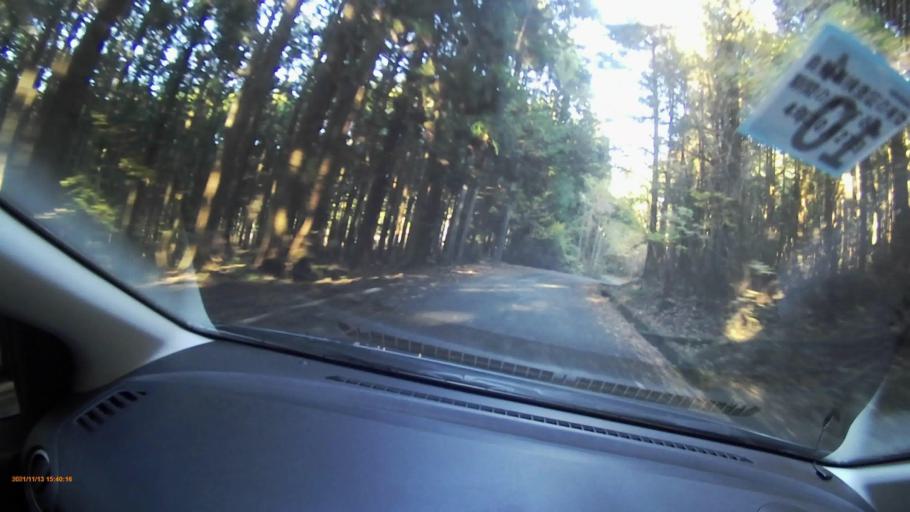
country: JP
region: Gifu
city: Nakatsugawa
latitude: 35.5823
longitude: 137.3878
